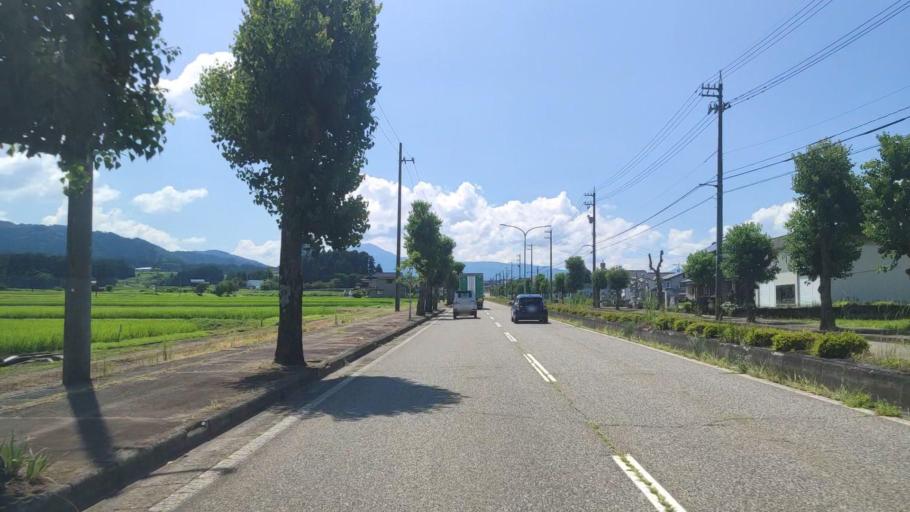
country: JP
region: Fukui
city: Katsuyama
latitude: 36.0481
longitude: 136.5155
